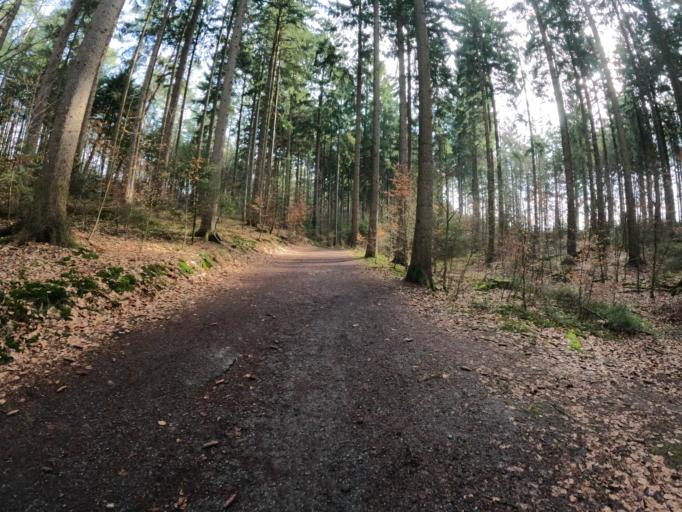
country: DE
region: Lower Saxony
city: Neu Wulmstorf
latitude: 53.4426
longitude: 9.8797
